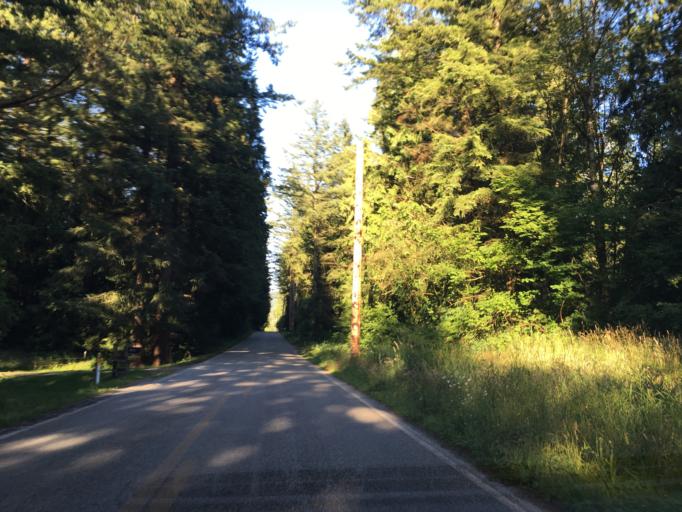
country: US
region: Washington
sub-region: Whatcom County
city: Nooksack
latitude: 48.9420
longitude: -122.2944
